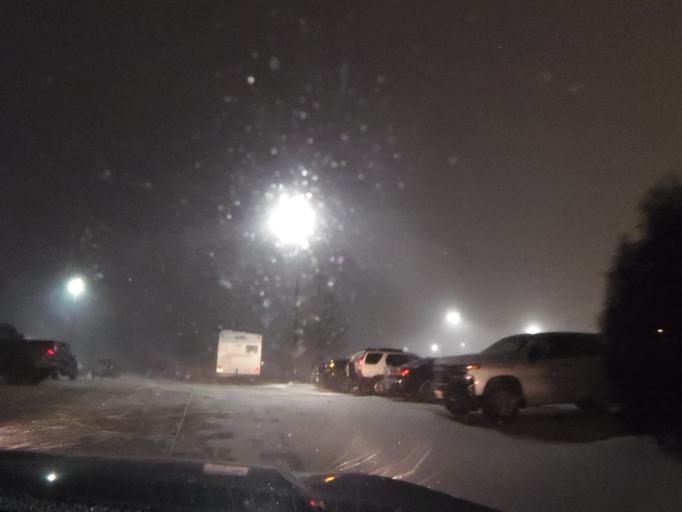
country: US
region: Minnesota
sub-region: Freeborn County
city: Albert Lea
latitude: 43.6595
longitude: -93.3127
